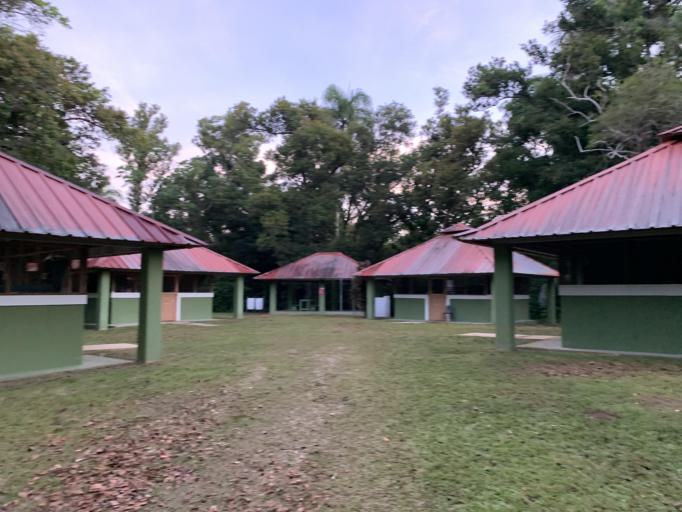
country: PR
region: San Sebastian
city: Juncal
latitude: 18.3710
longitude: -66.9198
